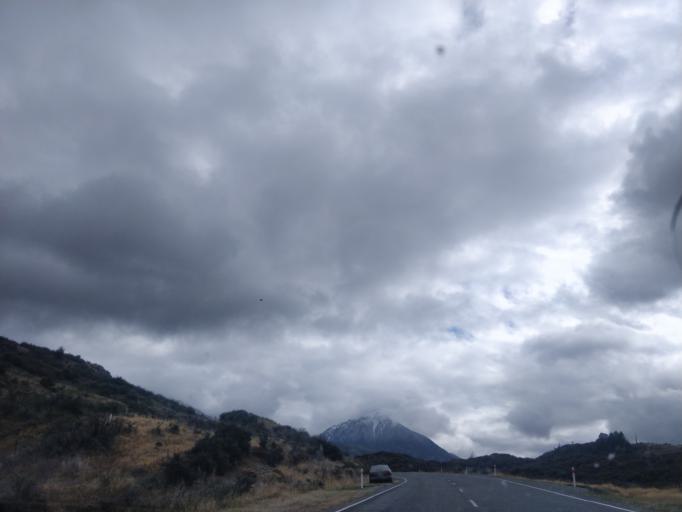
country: NZ
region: Canterbury
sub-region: Waimakariri District
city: Oxford
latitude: -43.0171
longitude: 171.7466
